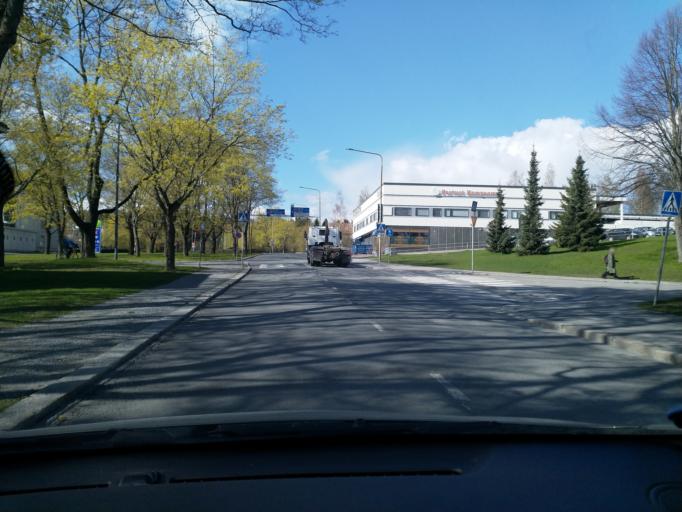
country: FI
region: Pirkanmaa
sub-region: Tampere
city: Tampere
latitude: 61.5040
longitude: 23.7870
